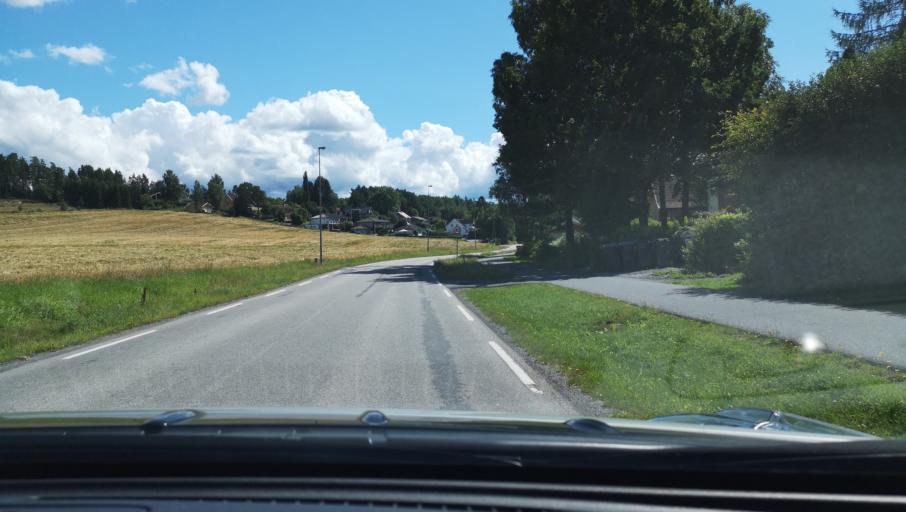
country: NO
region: Akershus
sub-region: As
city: As
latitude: 59.6573
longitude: 10.7988
